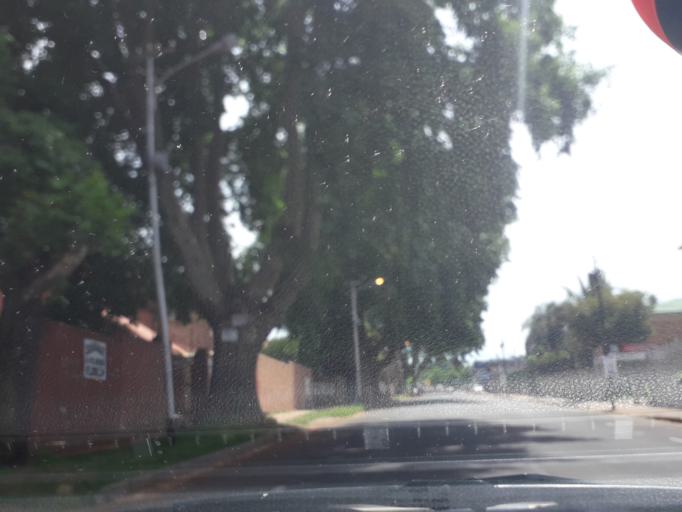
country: ZA
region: Gauteng
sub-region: City of Johannesburg Metropolitan Municipality
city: Roodepoort
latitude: -26.1769
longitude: 27.9108
